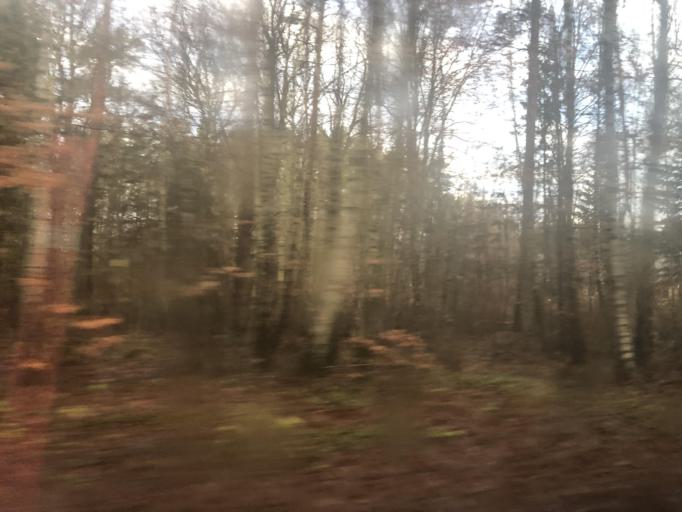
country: SE
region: Skane
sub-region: Sjobo Kommun
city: Blentarp
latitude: 55.6112
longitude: 13.5447
